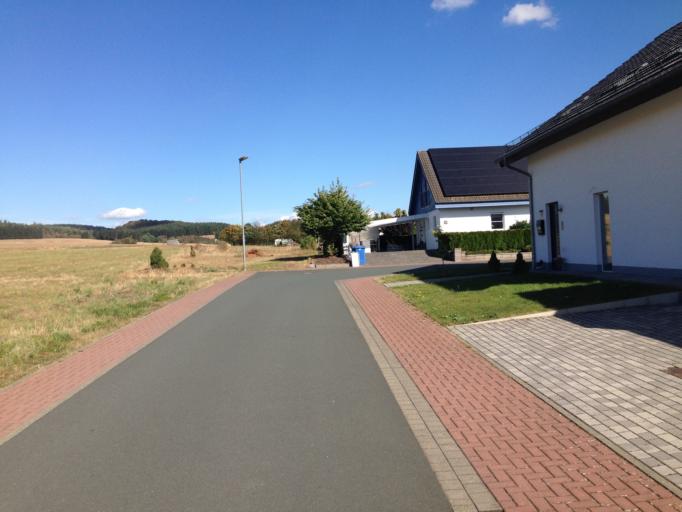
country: DE
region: Hesse
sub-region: Regierungsbezirk Giessen
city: Bischoffen
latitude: 50.6900
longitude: 8.4868
